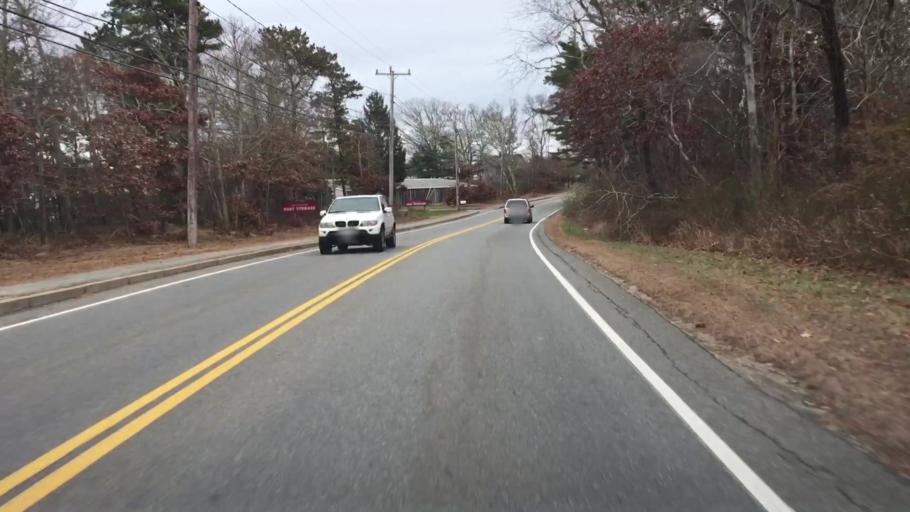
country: US
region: Massachusetts
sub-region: Barnstable County
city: Teaticket
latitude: 41.5829
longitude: -70.6047
